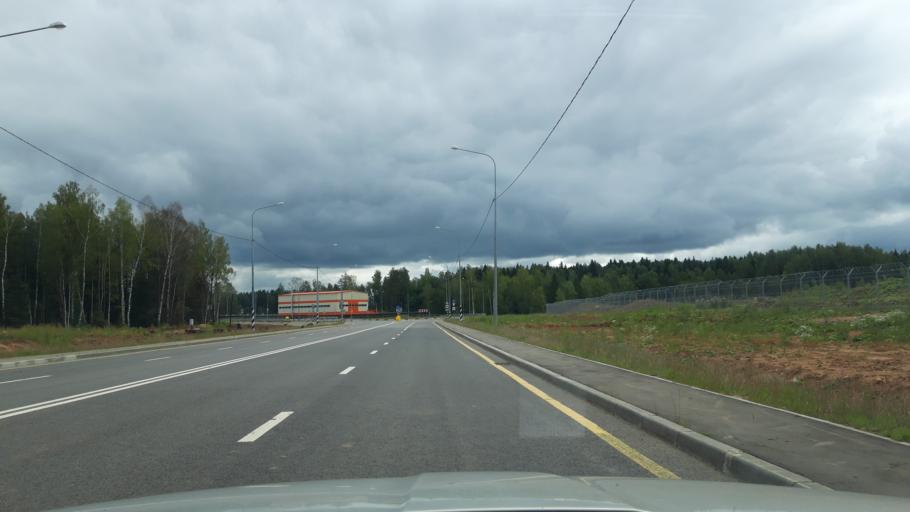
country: RU
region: Moskovskaya
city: Lozhki
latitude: 56.0816
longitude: 37.0890
